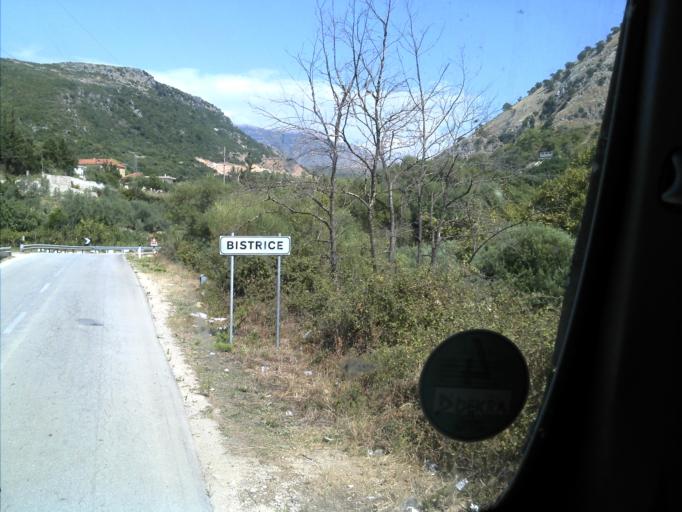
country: AL
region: Vlore
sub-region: Rrethi i Delvines
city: Mesopotam
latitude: 39.9154
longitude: 20.1325
